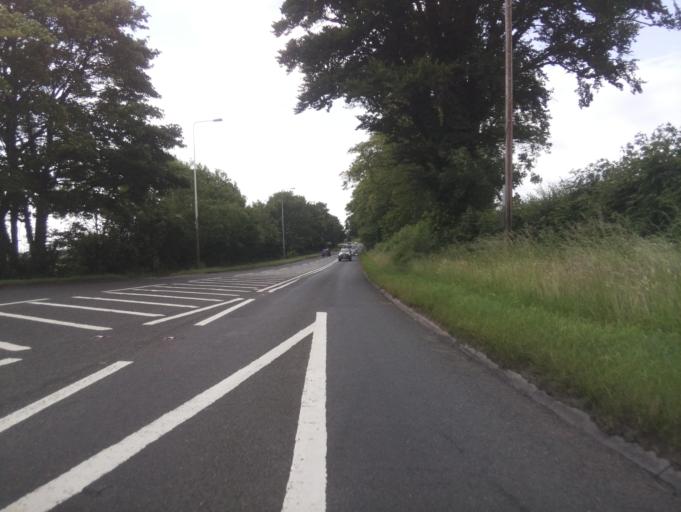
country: GB
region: Wales
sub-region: Vale of Glamorgan
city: Barry
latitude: 51.4629
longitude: -3.2926
